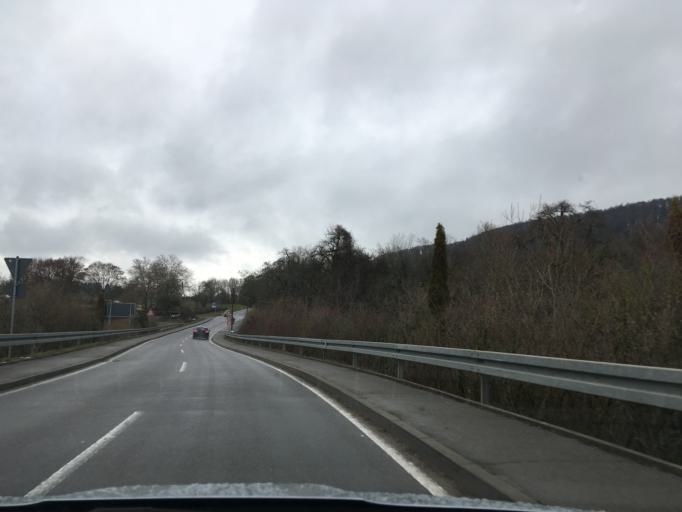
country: DE
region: Baden-Wuerttemberg
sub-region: Freiburg Region
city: Gottmadingen
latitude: 47.7378
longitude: 8.7695
